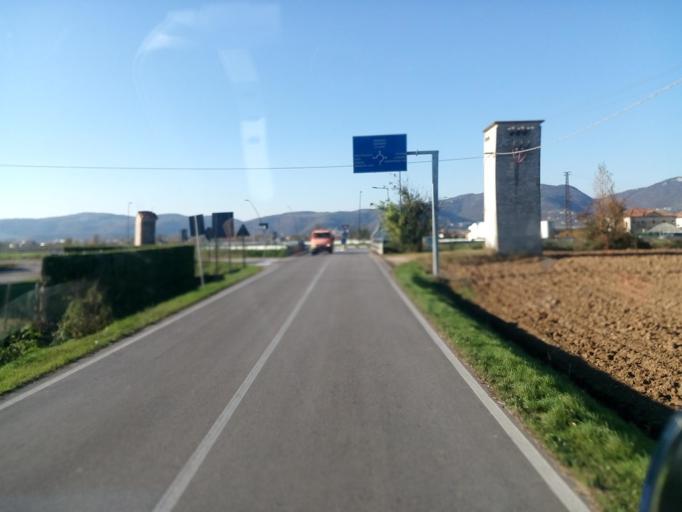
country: IT
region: Veneto
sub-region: Provincia di Vicenza
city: Ponte di Barbarano
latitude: 45.3843
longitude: 11.5727
